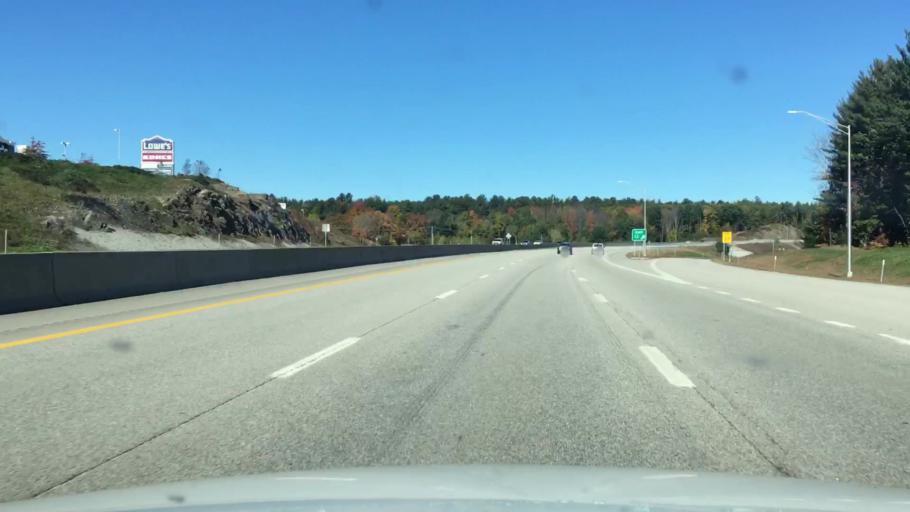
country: US
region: New Hampshire
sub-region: Strafford County
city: Rochester
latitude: 43.2927
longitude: -70.9914
